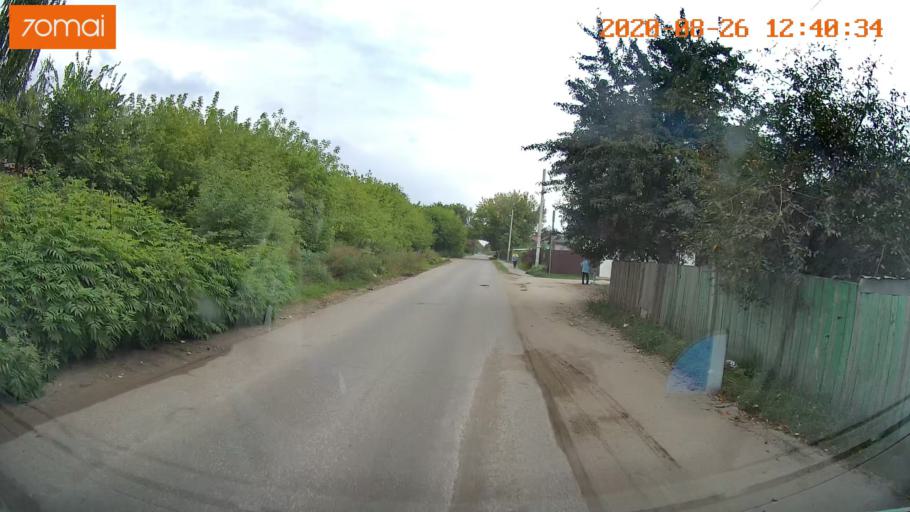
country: RU
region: Rjazan
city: Ryazan'
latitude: 54.6010
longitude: 39.7601
